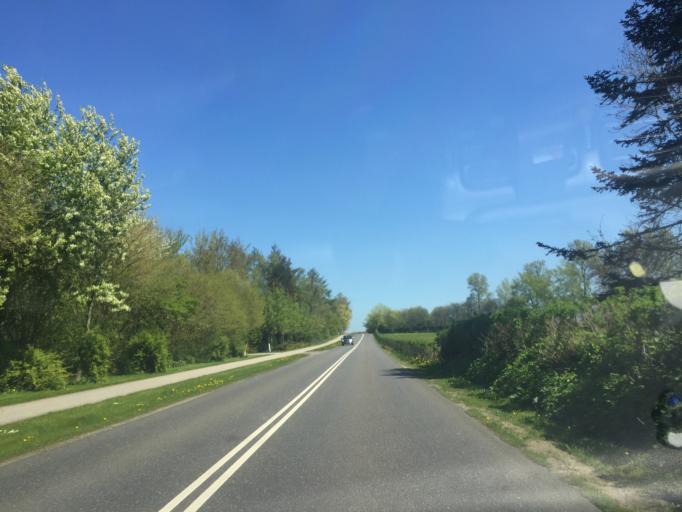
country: DK
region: Capital Region
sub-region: Egedal Kommune
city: Ganlose
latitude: 55.7838
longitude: 12.2492
